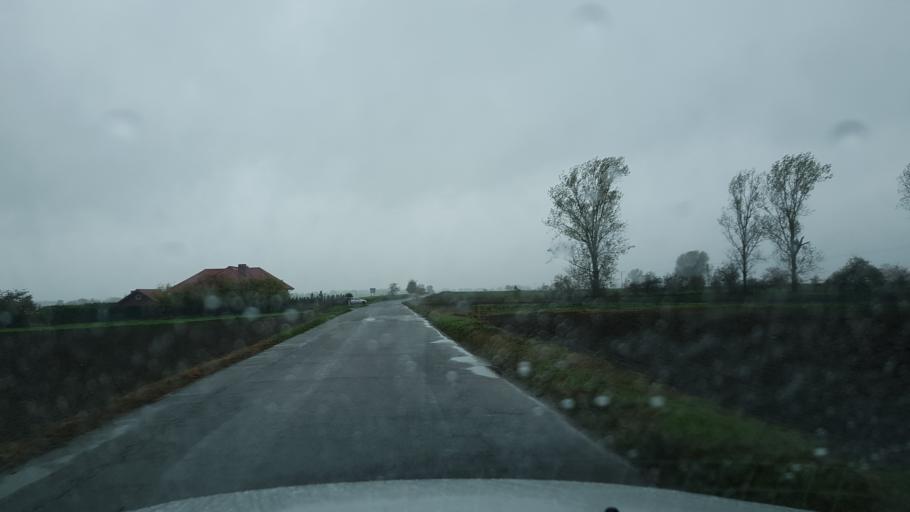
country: PL
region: West Pomeranian Voivodeship
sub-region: Powiat pyrzycki
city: Kozielice
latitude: 53.1634
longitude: 14.8327
